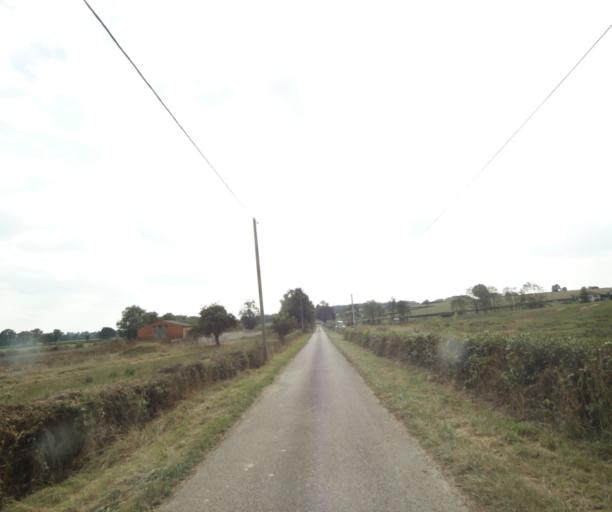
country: FR
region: Bourgogne
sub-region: Departement de Saone-et-Loire
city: Palinges
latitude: 46.5119
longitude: 4.1838
